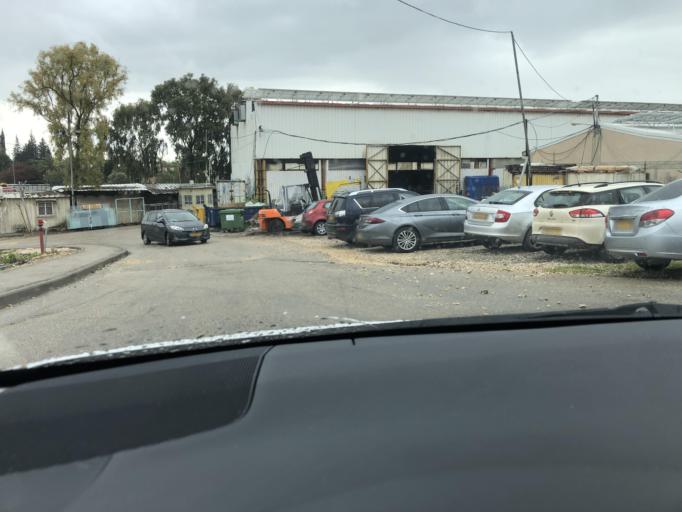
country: PS
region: West Bank
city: Mashah
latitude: 32.1110
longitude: 35.0392
